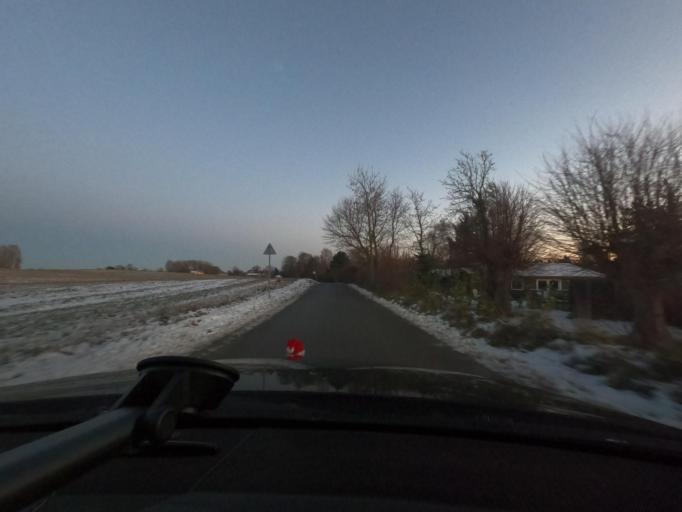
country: DK
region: South Denmark
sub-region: Sonderborg Kommune
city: Horuphav
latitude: 54.8608
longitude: 9.9240
